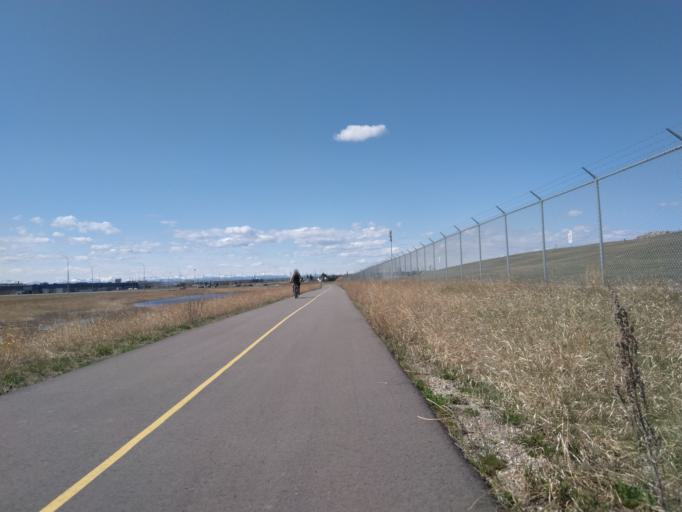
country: CA
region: Alberta
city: Chestermere
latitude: 51.0159
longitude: -113.9508
